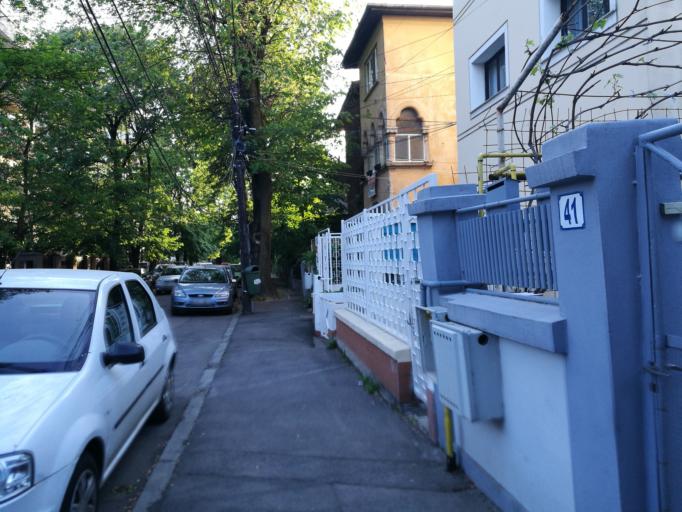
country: RO
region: Bucuresti
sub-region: Municipiul Bucuresti
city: Bucuresti
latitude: 44.4679
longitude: 26.0666
